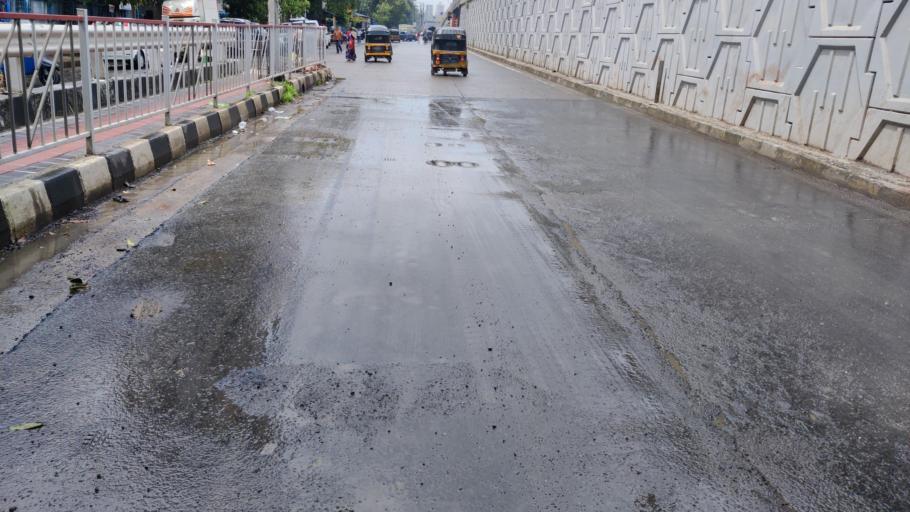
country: IN
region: Maharashtra
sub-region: Mumbai Suburban
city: Borivli
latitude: 19.2454
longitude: 72.8649
